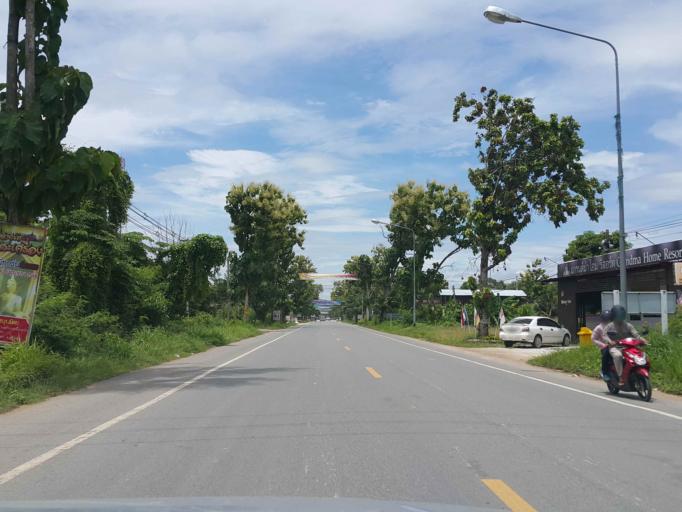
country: TH
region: Sukhothai
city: Ban Na
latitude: 17.0165
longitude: 99.7301
